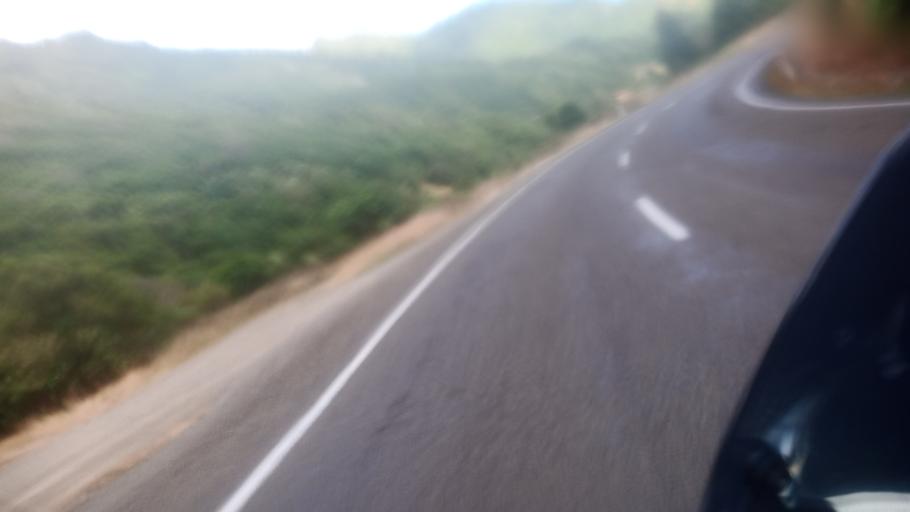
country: NZ
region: Bay of Plenty
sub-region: Opotiki District
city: Opotiki
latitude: -38.3352
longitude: 177.4195
